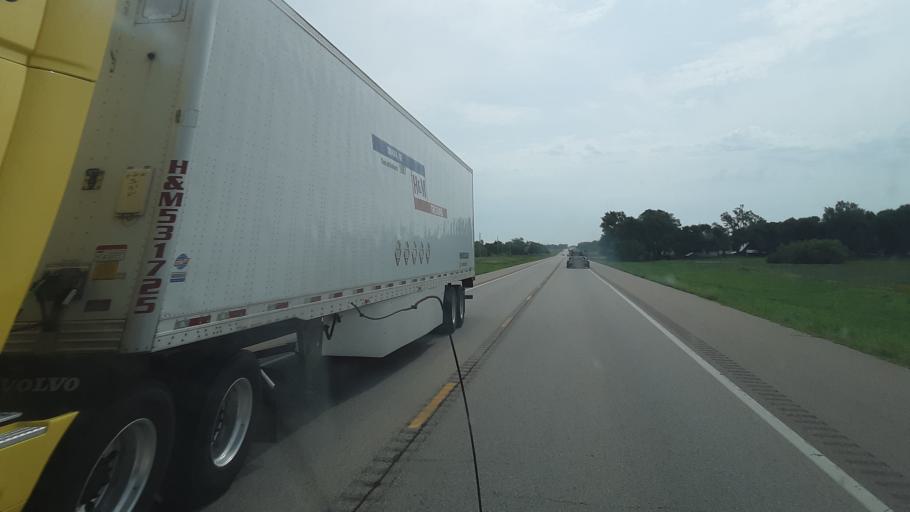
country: US
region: Kansas
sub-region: Stafford County
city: Stafford
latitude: 37.9842
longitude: -98.3426
